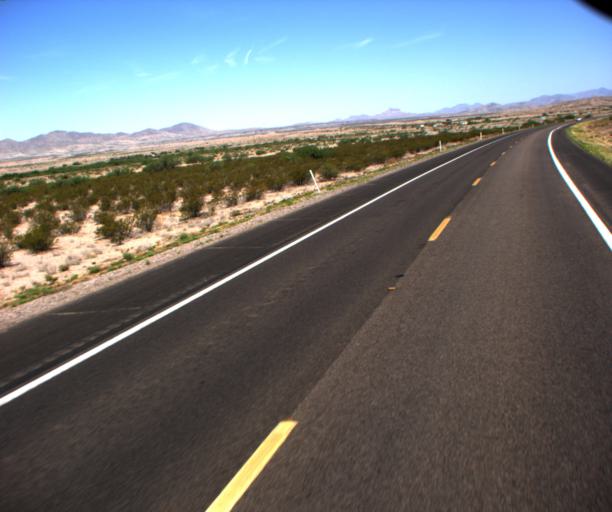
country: US
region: Arizona
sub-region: Greenlee County
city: Clifton
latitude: 32.6591
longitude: -109.0686
